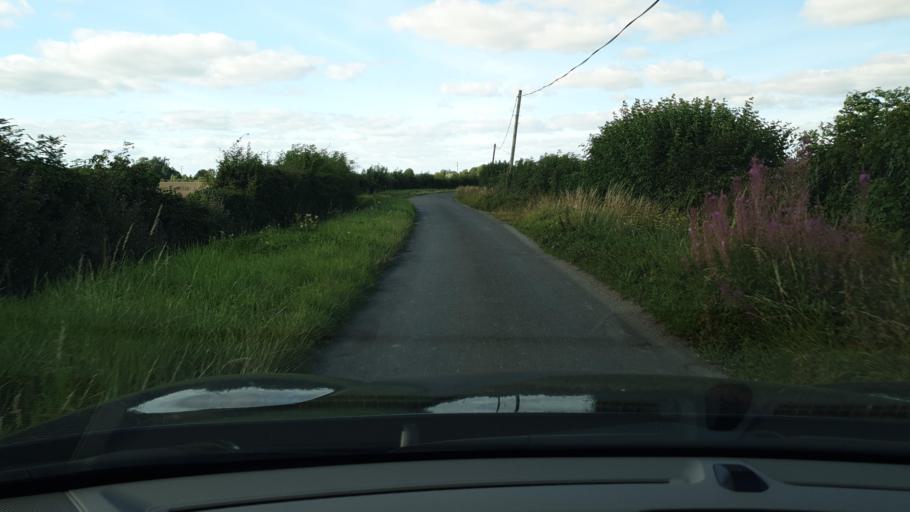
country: IE
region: Leinster
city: Hartstown
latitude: 53.4386
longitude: -6.4308
